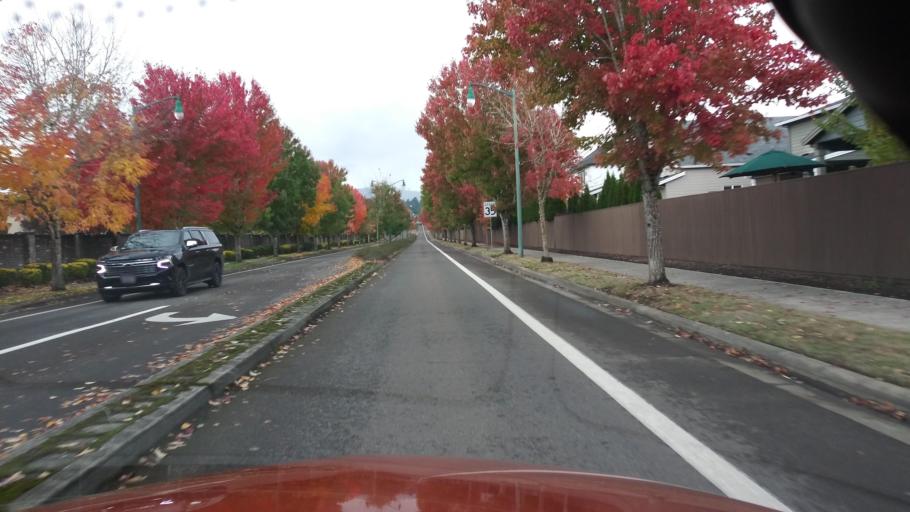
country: US
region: Oregon
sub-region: Washington County
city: Forest Grove
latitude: 45.5393
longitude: -123.1244
